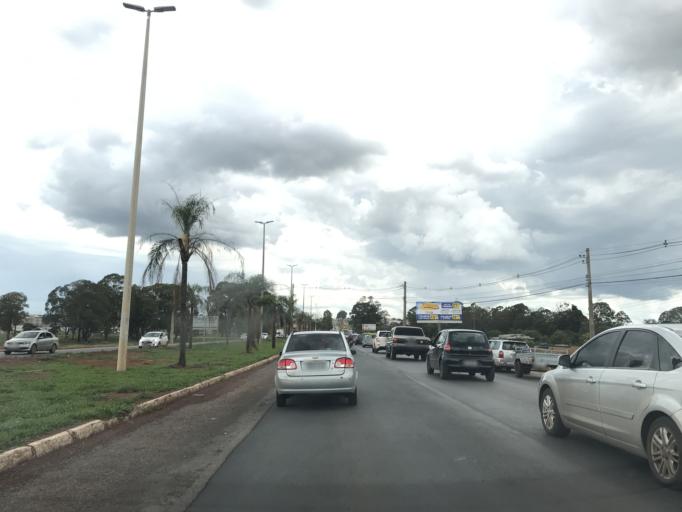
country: BR
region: Federal District
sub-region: Brasilia
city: Brasilia
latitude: -15.8874
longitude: -48.0589
